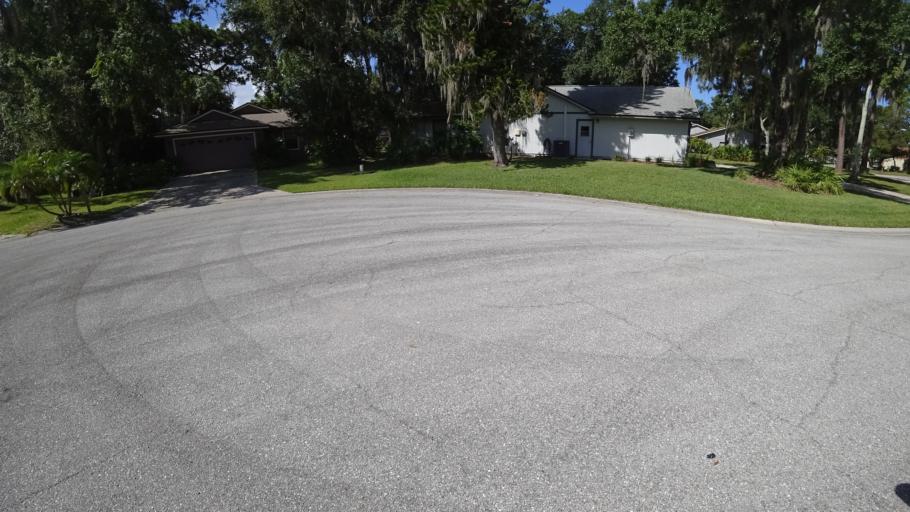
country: US
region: Florida
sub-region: Sarasota County
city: Desoto Lakes
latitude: 27.3969
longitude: -82.4986
